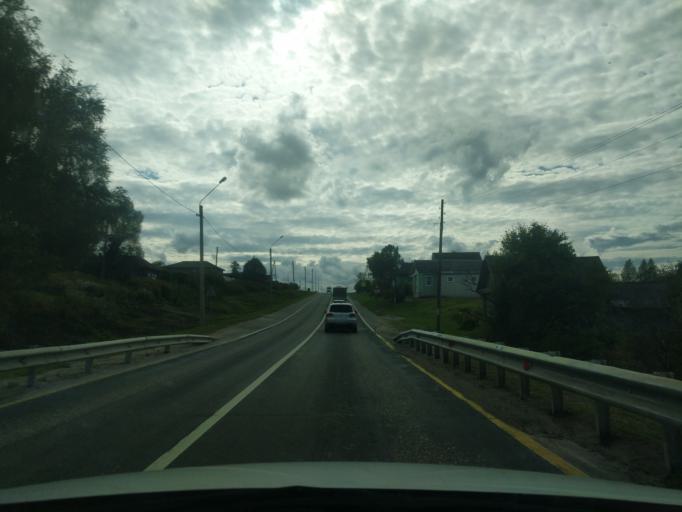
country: RU
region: Jaroslavl
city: Levashevo
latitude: 57.6550
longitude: 40.5610
